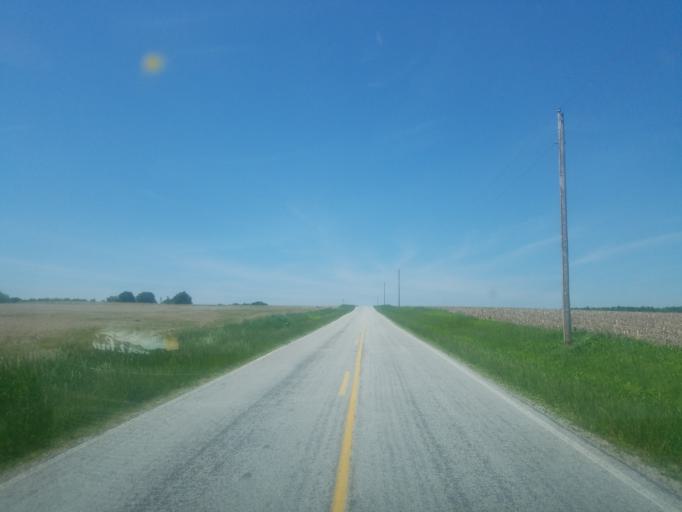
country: US
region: Ohio
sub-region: Huron County
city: New London
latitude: 41.1109
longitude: -82.4569
